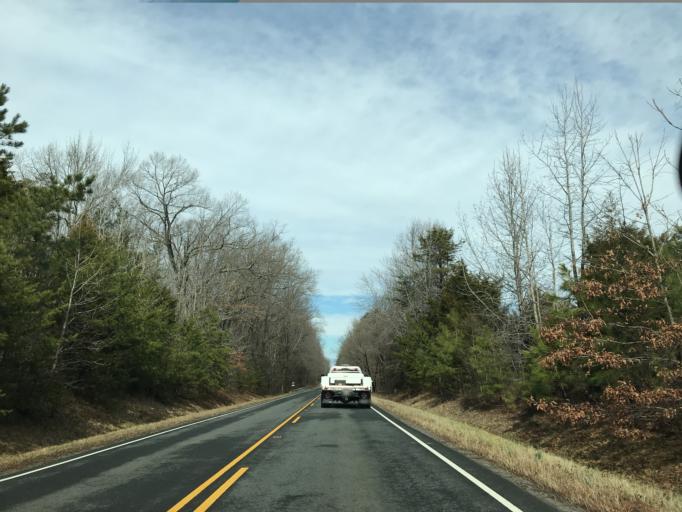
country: US
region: Virginia
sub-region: King George County
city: Dahlgren
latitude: 38.3023
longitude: -77.0740
